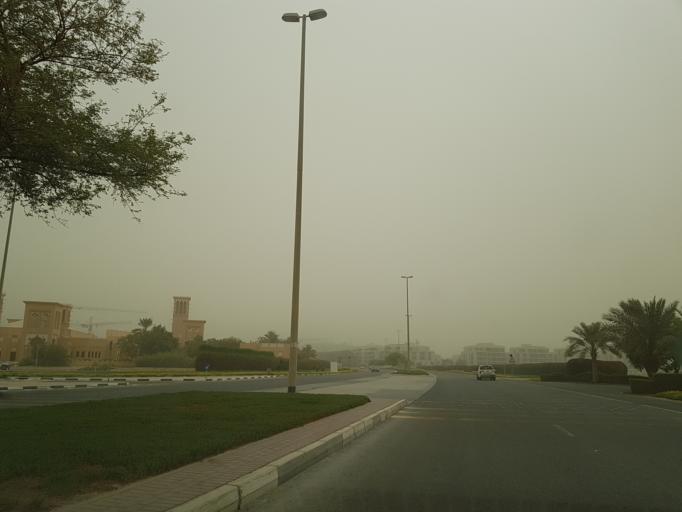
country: AE
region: Dubai
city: Dubai
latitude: 25.1510
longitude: 55.2891
